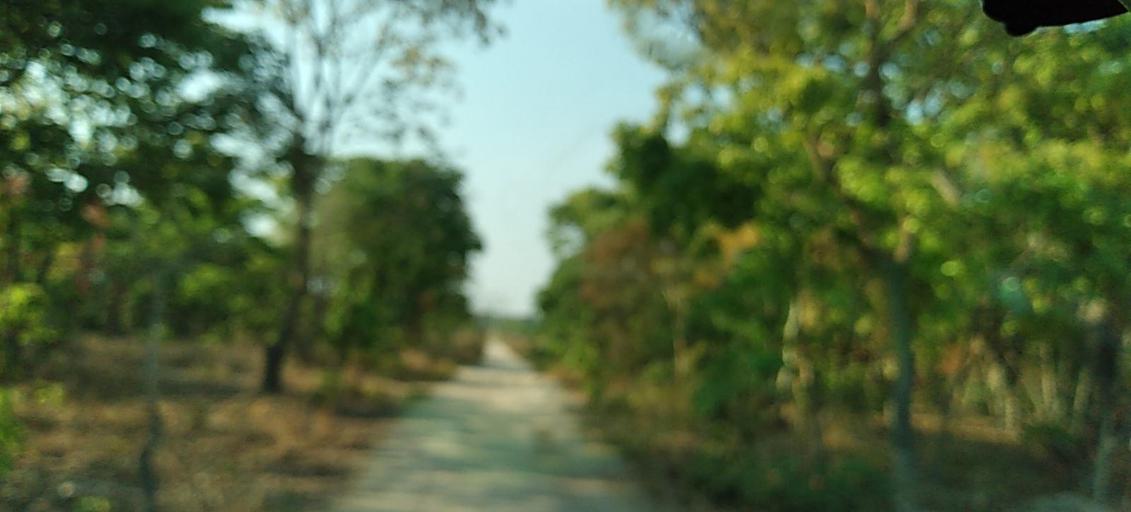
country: ZM
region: North-Western
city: Kalengwa
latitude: -13.1620
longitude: 25.0347
